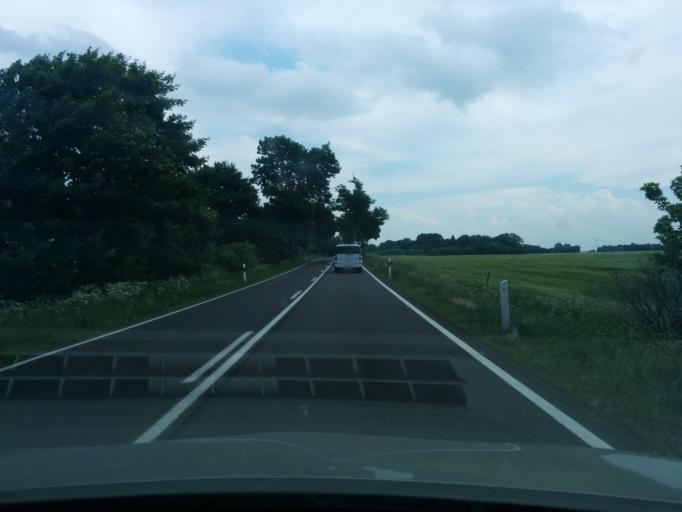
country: DE
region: Mecklenburg-Vorpommern
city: Jarmen
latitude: 53.9454
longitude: 13.3818
